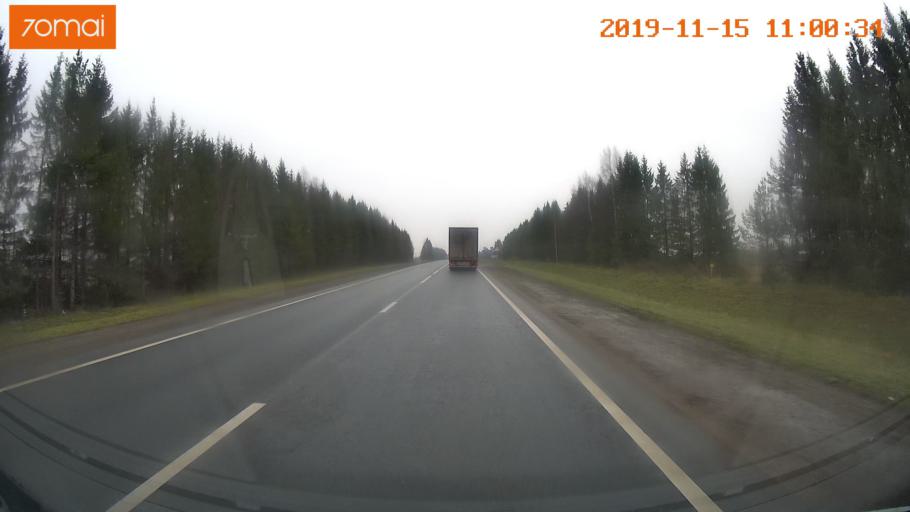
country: RU
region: Vologda
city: Chebsara
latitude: 59.1364
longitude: 38.9026
